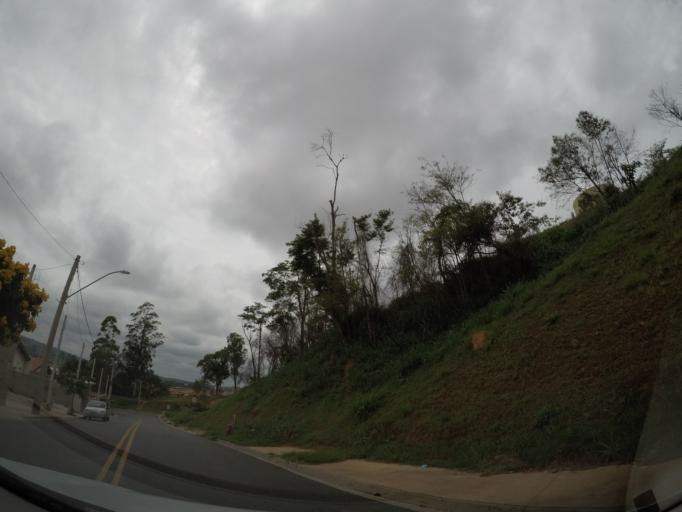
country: BR
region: Sao Paulo
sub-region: Louveira
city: Louveira
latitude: -23.0858
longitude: -46.9889
